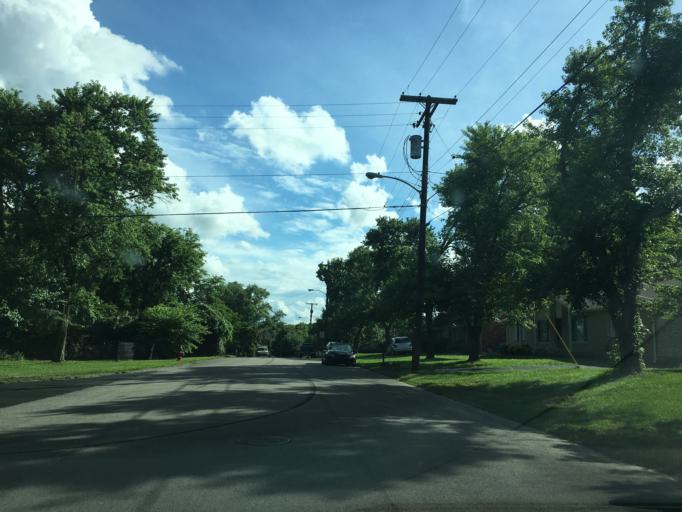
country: US
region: Tennessee
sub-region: Davidson County
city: Oak Hill
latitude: 36.0925
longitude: -86.7242
